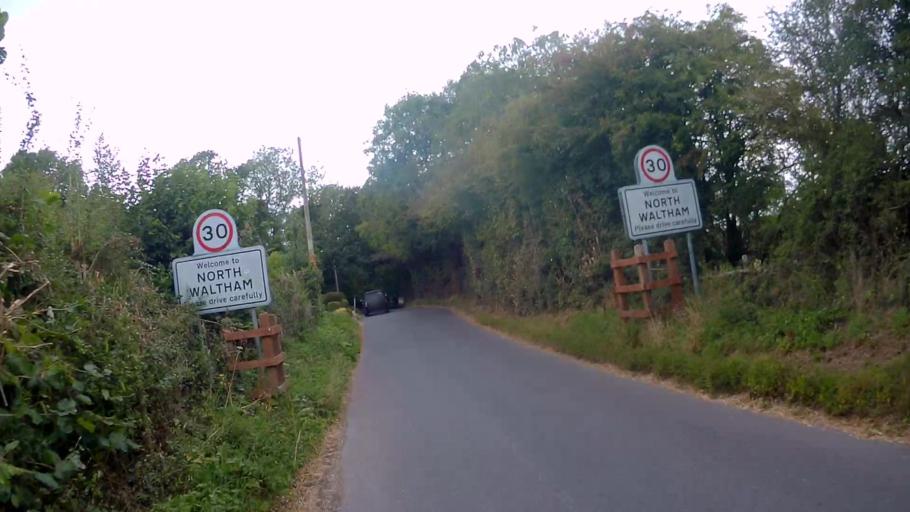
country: GB
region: England
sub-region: Hampshire
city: Overton
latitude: 51.2096
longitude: -1.1930
